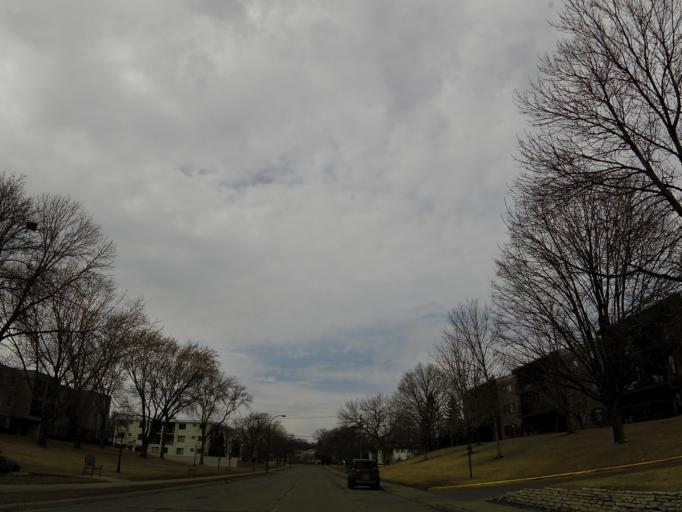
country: US
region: Minnesota
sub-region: Hennepin County
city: Edina
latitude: 44.8684
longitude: -93.3325
